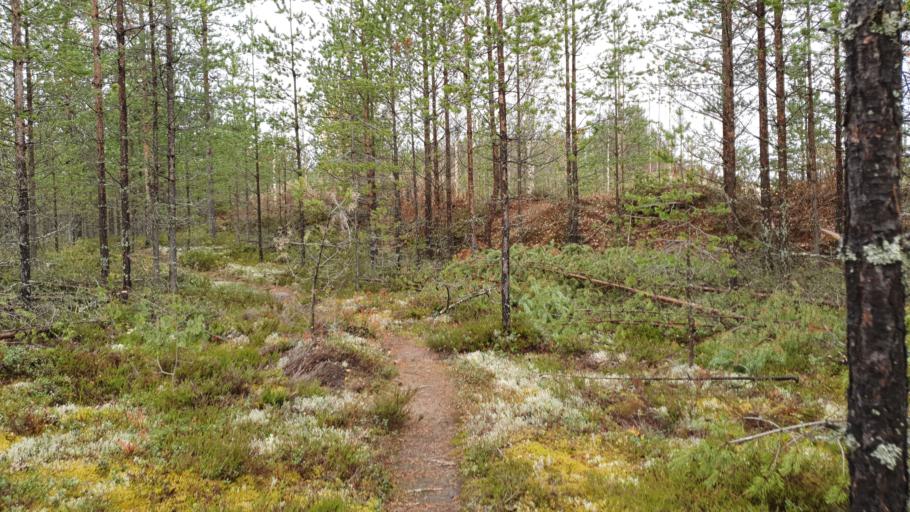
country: FI
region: Kainuu
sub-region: Kehys-Kainuu
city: Kuhmo
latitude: 64.1494
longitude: 29.4011
